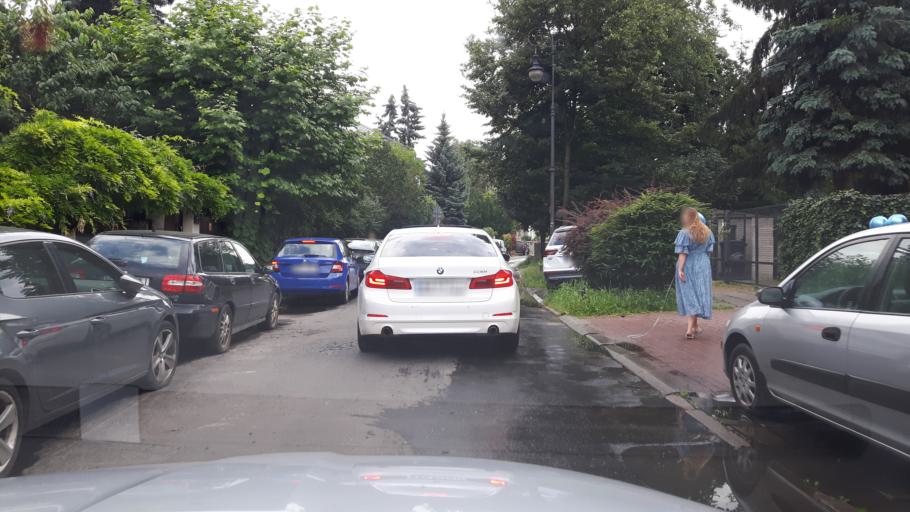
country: PL
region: Masovian Voivodeship
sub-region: Warszawa
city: Praga Polnoc
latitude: 52.2303
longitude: 21.0548
